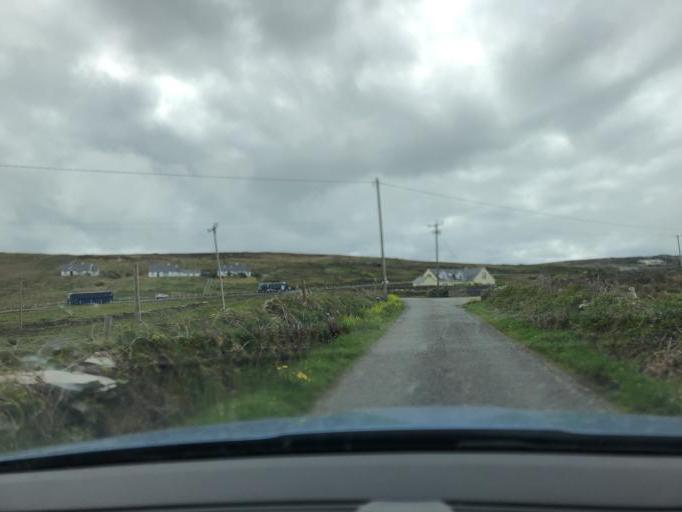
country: IE
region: Munster
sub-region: An Clar
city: Kilrush
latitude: 52.9922
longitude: -9.4058
